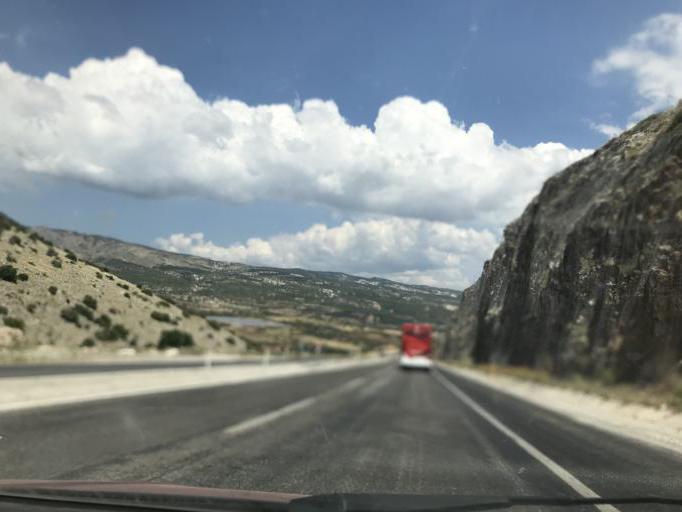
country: TR
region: Denizli
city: Serinhisar
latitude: 37.6203
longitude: 29.2592
